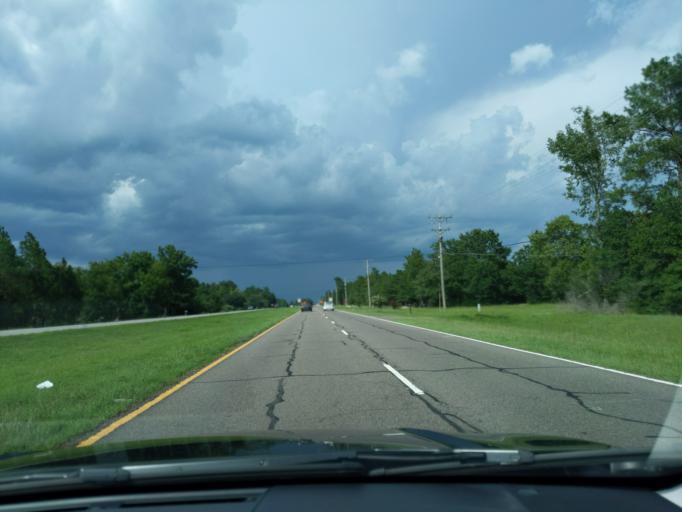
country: US
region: South Carolina
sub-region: Edgefield County
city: Murphys Estates
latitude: 33.6414
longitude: -81.9076
